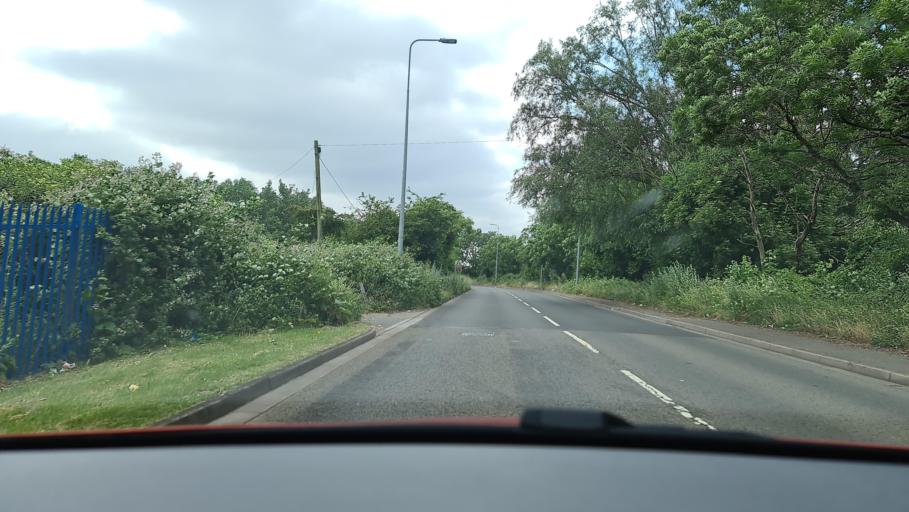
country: GB
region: Wales
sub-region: Cardiff
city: Cardiff
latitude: 51.5002
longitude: -3.1238
